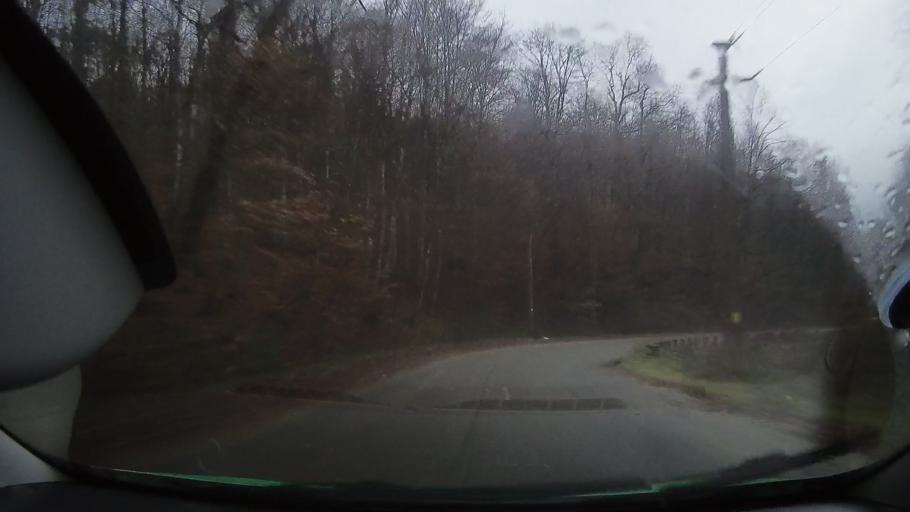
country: RO
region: Hunedoara
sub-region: Comuna Ribita
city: Ribita
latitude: 46.2492
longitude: 22.7496
